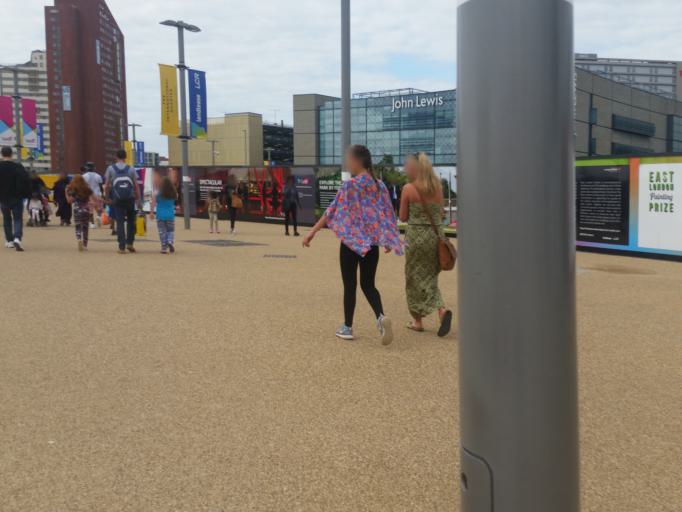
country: GB
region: England
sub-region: Greater London
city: Poplar
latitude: 51.5419
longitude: -0.0102
